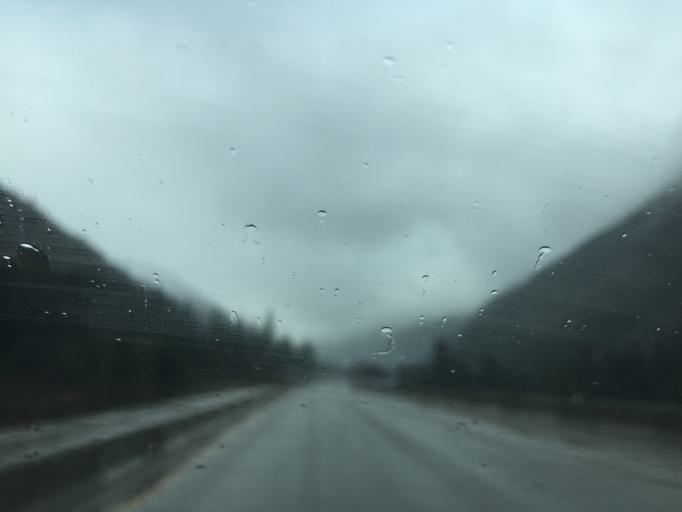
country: CA
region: British Columbia
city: Hope
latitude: 49.5620
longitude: -121.1869
